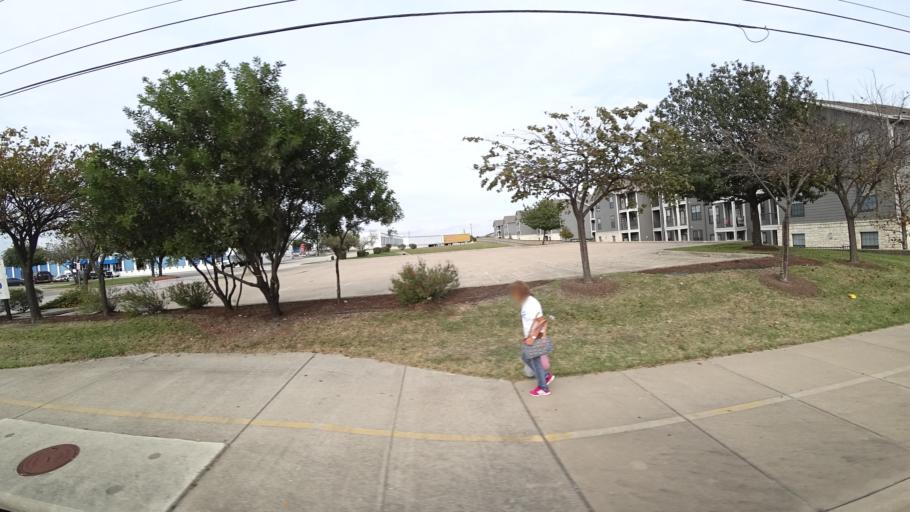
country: US
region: Texas
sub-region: Travis County
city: Wells Branch
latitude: 30.4234
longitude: -97.6688
